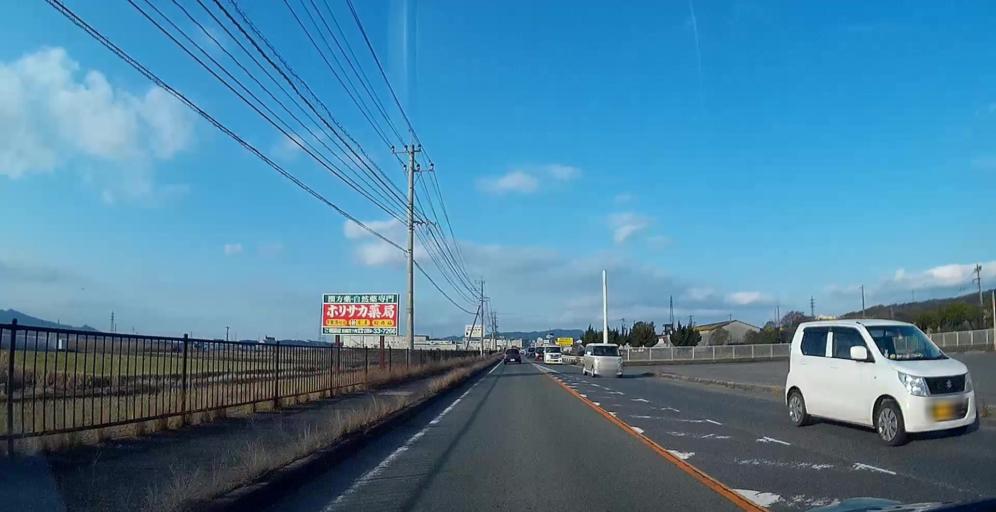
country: JP
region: Kumamoto
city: Matsubase
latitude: 32.6164
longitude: 130.7045
